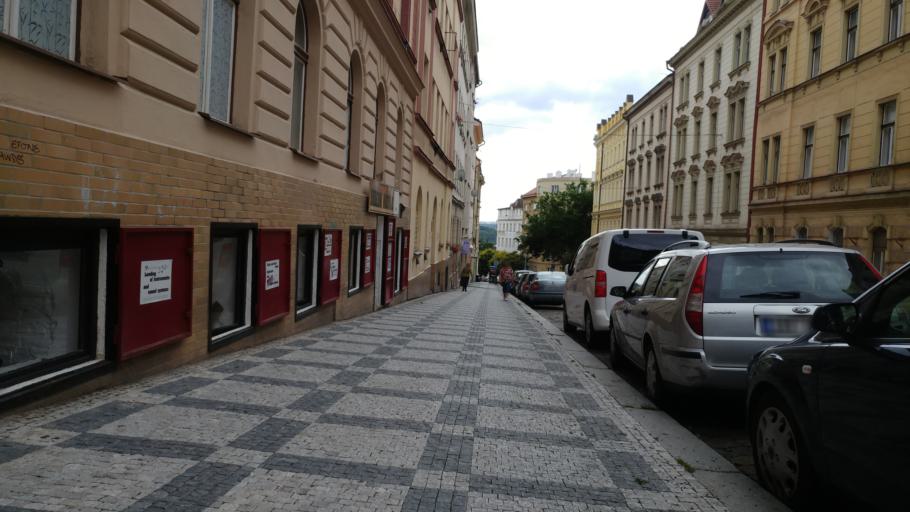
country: CZ
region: Praha
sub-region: Praha 8
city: Karlin
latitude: 50.0723
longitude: 14.4427
